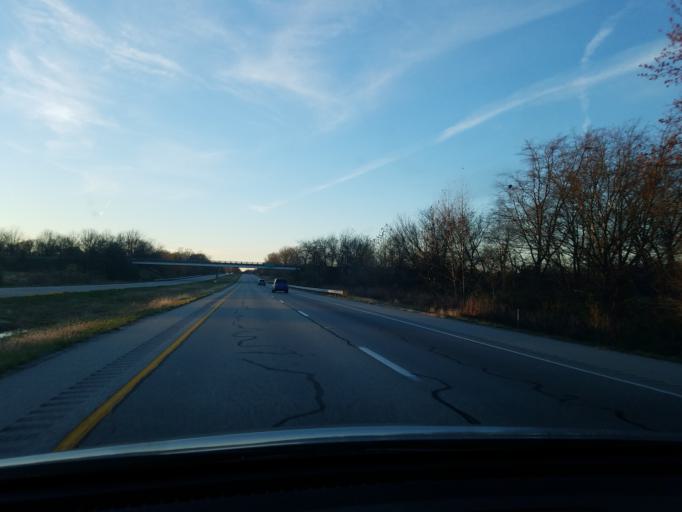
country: US
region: Indiana
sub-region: Posey County
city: Poseyville
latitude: 38.1872
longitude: -87.8263
